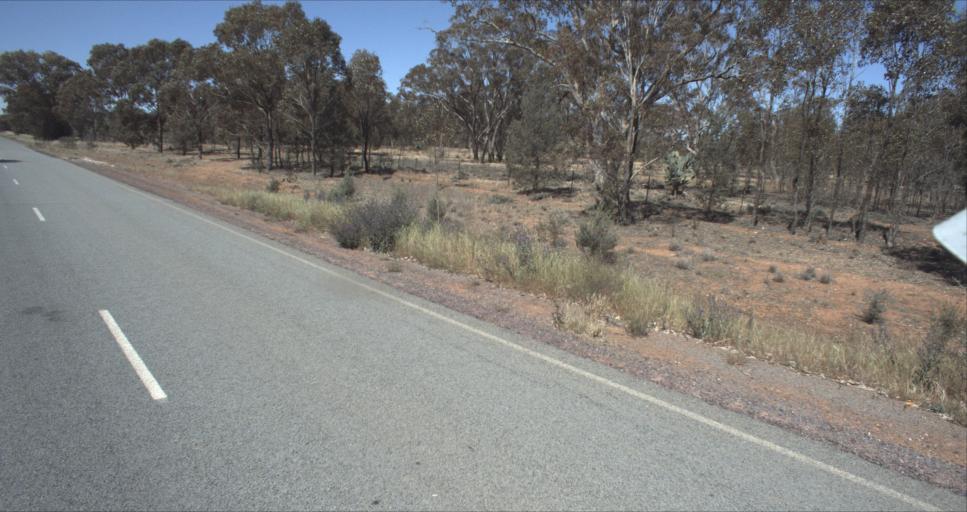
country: AU
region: New South Wales
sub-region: Leeton
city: Leeton
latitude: -34.4910
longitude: 146.4647
